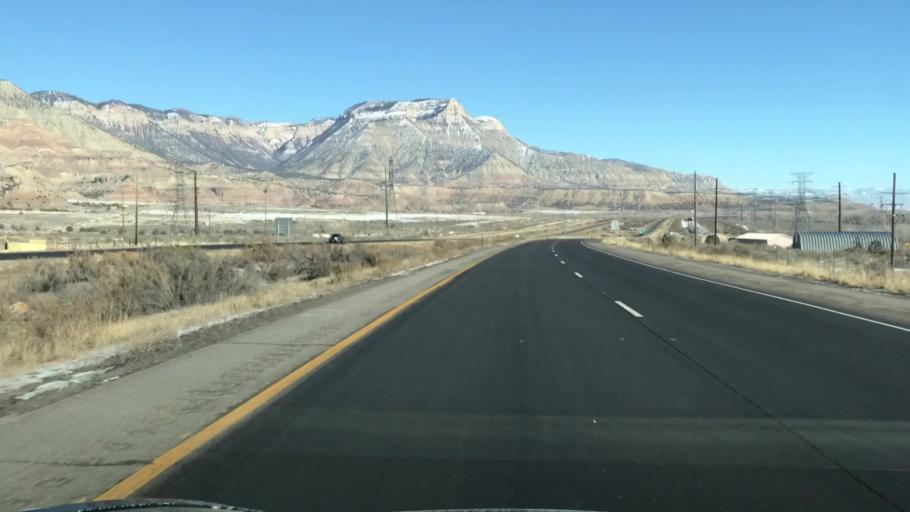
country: US
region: Colorado
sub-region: Garfield County
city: Parachute
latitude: 39.4622
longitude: -108.0422
